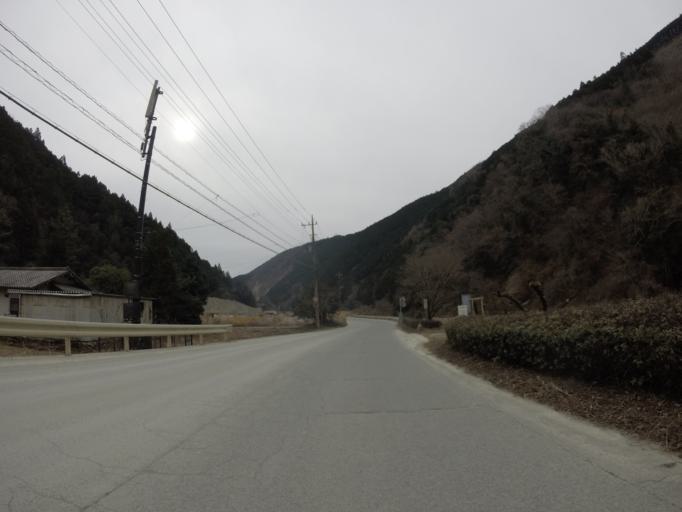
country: JP
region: Shizuoka
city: Fujinomiya
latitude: 35.2467
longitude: 138.5290
